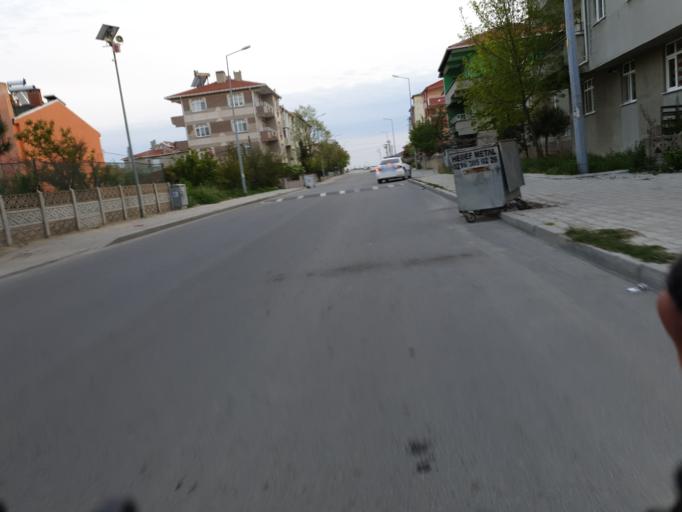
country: TR
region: Tekirdag
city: Saray
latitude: 41.4356
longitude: 27.9142
